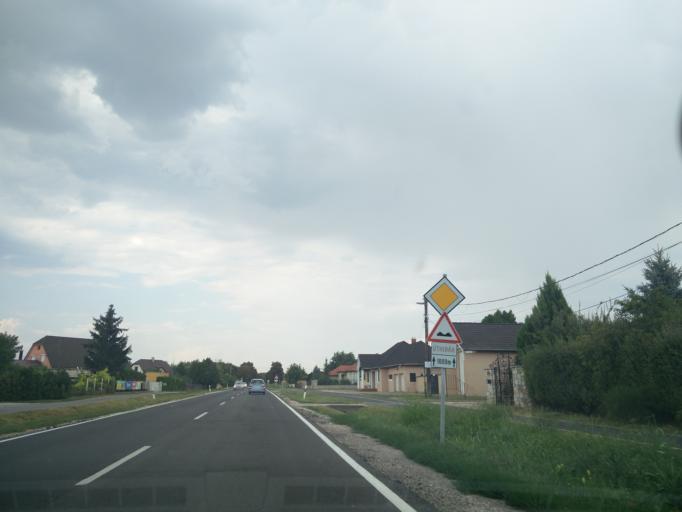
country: HU
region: Fejer
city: Polgardi
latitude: 47.0597
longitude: 18.3076
